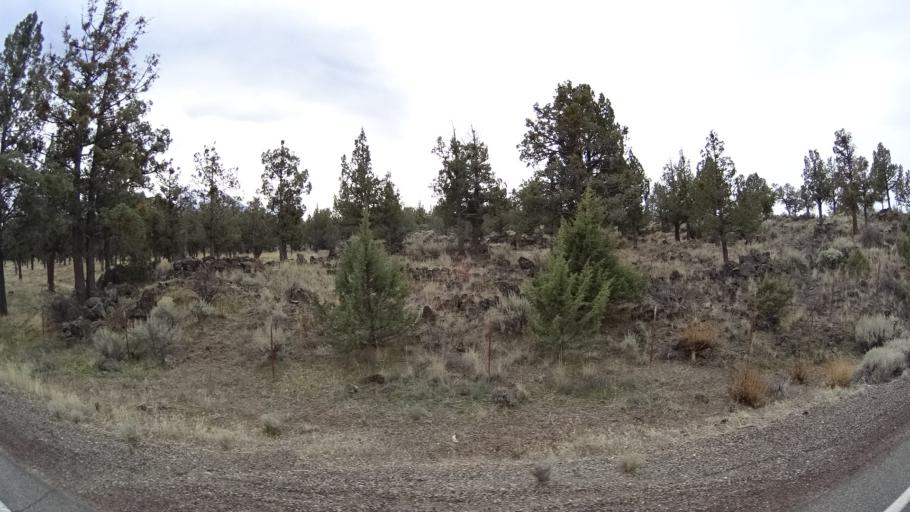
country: US
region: California
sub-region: Siskiyou County
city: Weed
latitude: 41.5930
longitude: -122.3113
